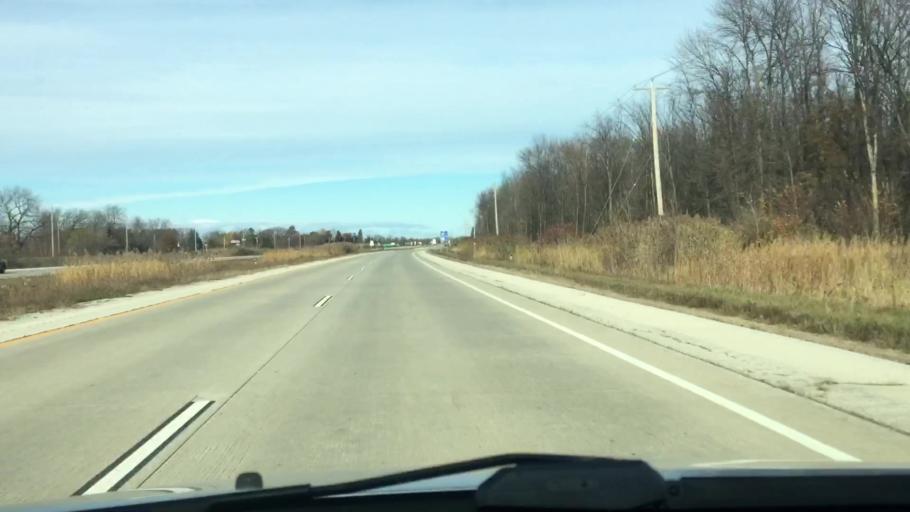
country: US
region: Wisconsin
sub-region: Brown County
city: Bellevue
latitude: 44.5700
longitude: -87.8775
